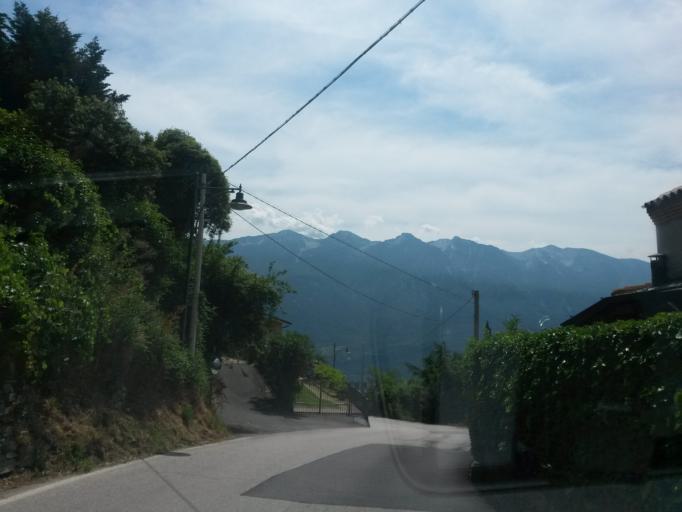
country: IT
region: Lombardy
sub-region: Provincia di Brescia
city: Pieve
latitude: 45.7823
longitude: 10.7645
